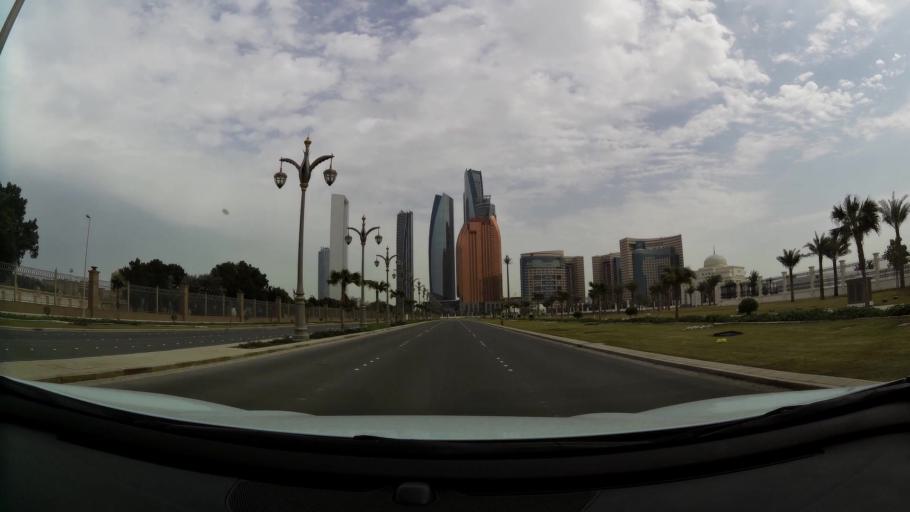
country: AE
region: Abu Dhabi
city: Abu Dhabi
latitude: 24.4572
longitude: 54.3129
